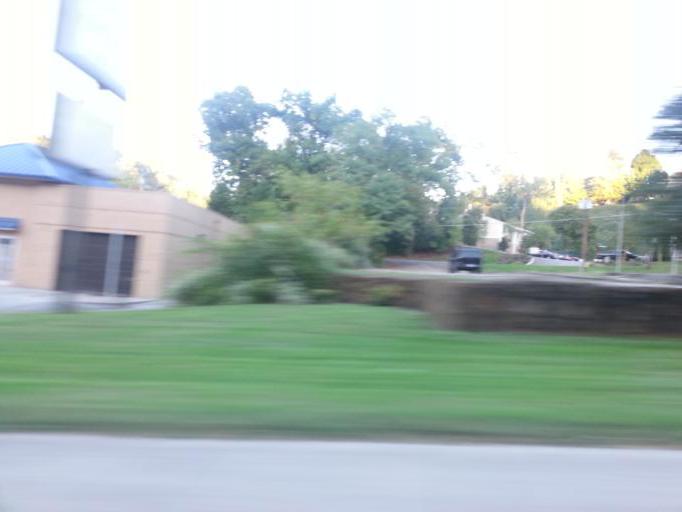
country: US
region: Tennessee
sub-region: Knox County
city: Knoxville
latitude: 35.9475
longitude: -83.9128
